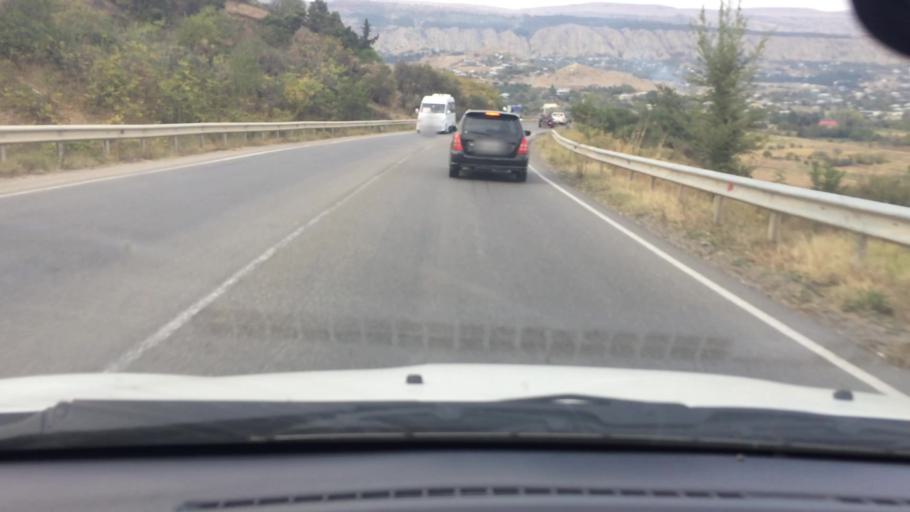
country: GE
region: T'bilisi
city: Tbilisi
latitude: 41.5952
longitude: 44.7799
